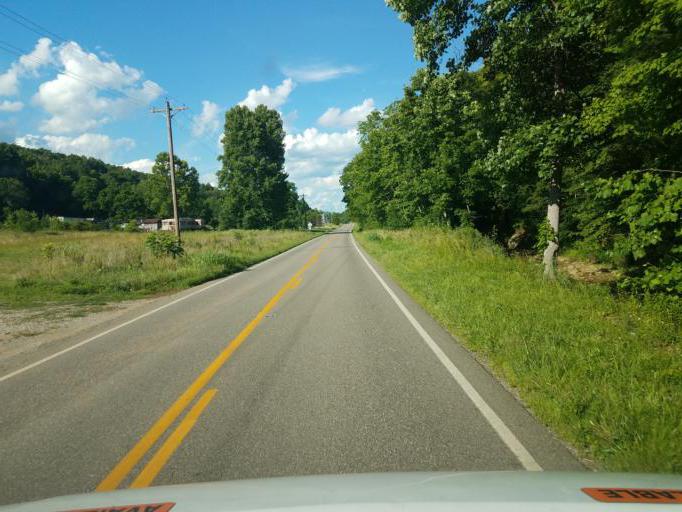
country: US
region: Ohio
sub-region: Gallia County
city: Gallipolis
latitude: 38.7787
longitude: -82.3510
